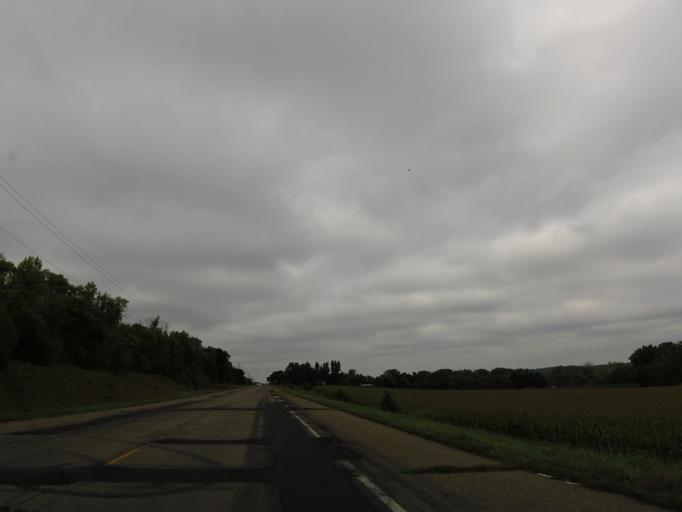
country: US
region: Minnesota
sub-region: Yellow Medicine County
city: Granite Falls
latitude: 44.8422
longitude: -95.6146
